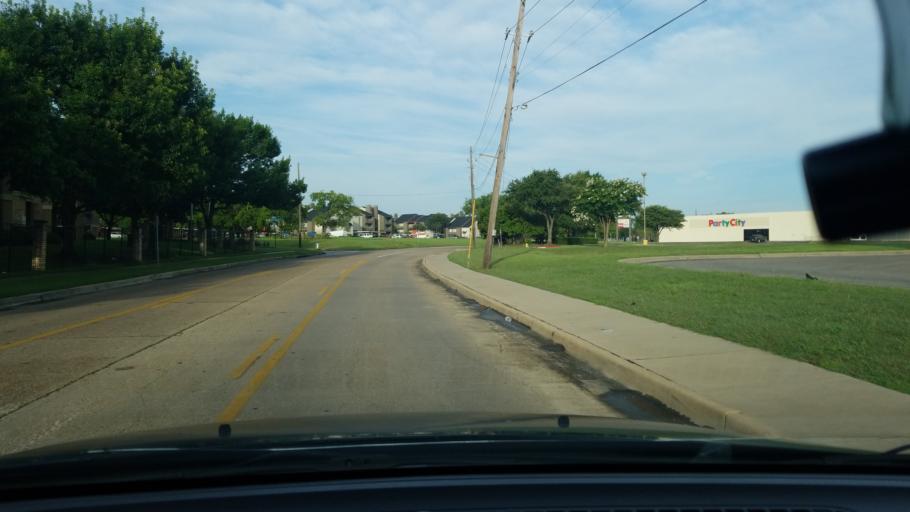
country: US
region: Texas
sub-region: Dallas County
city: Mesquite
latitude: 32.8071
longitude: -96.6148
